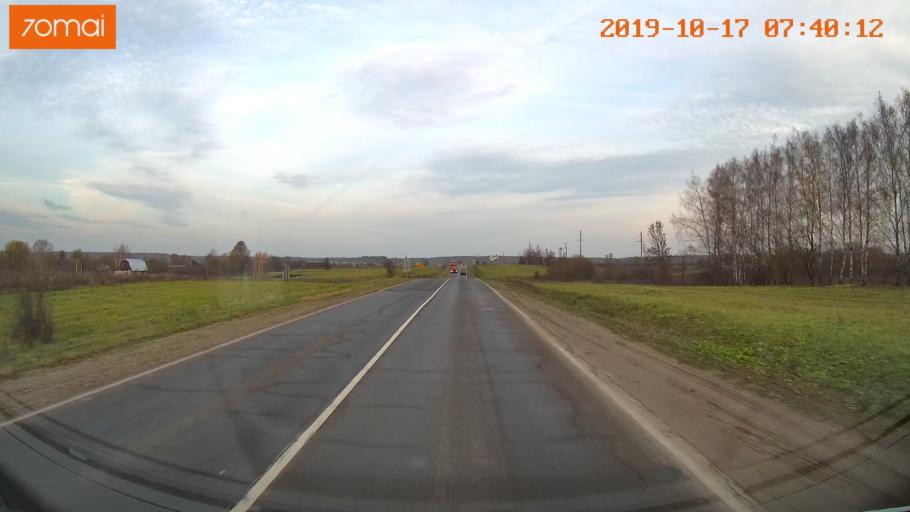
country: RU
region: Vladimir
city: Yur'yev-Pol'skiy
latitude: 56.4703
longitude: 39.8344
